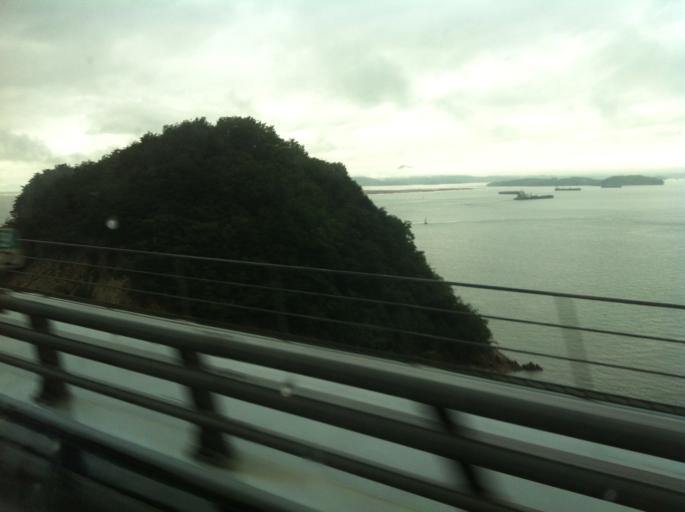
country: KR
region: Gyeonggi-do
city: Tongjin
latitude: 37.5475
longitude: 126.5898
